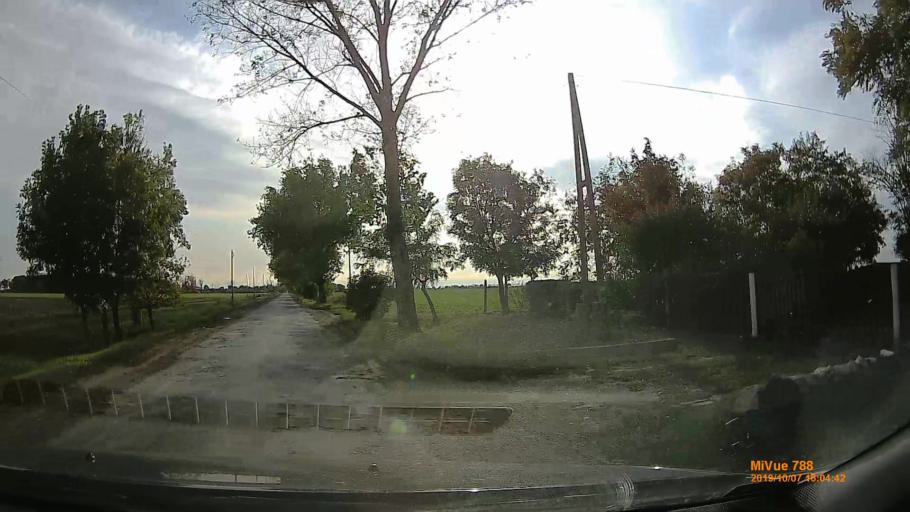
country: HU
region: Bekes
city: Szarvas
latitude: 46.8026
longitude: 20.6364
